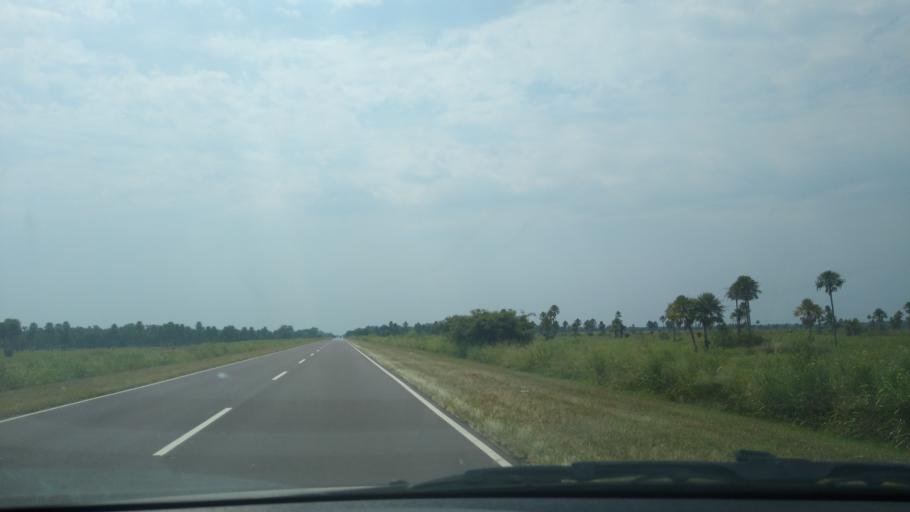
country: AR
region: Chaco
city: La Eduvigis
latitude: -27.0343
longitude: -58.9651
